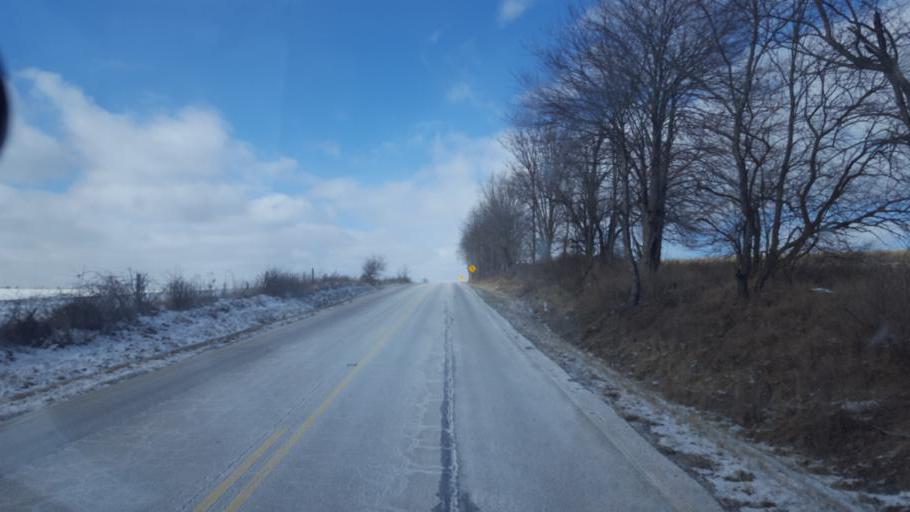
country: US
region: Ohio
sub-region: Knox County
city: Oak Hill
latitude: 40.3345
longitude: -82.1873
